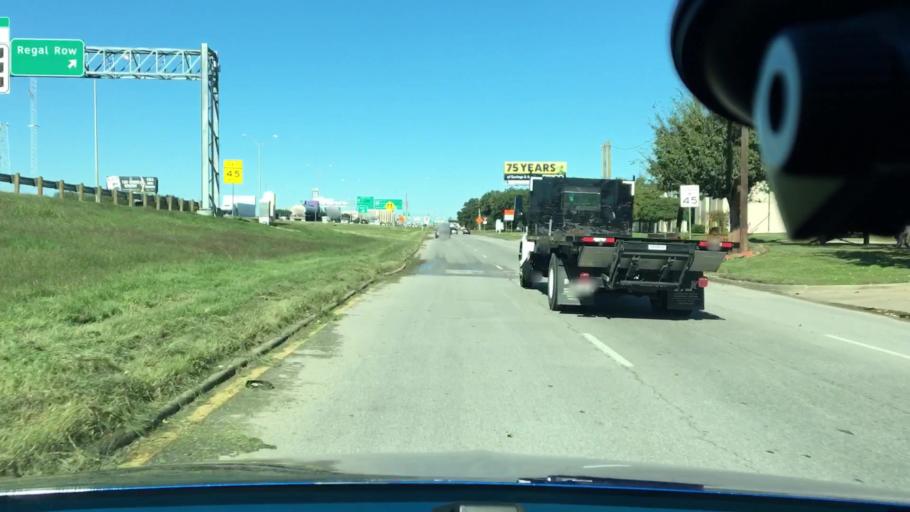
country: US
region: Texas
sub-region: Dallas County
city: Dallas
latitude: 32.8185
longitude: -96.8719
